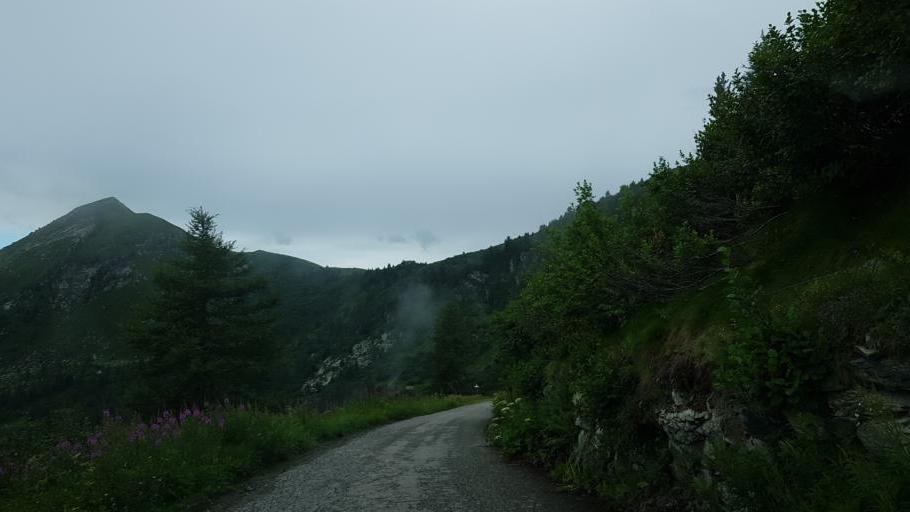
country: IT
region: Piedmont
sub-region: Provincia di Cuneo
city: Serre
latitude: 44.5511
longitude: 7.1262
